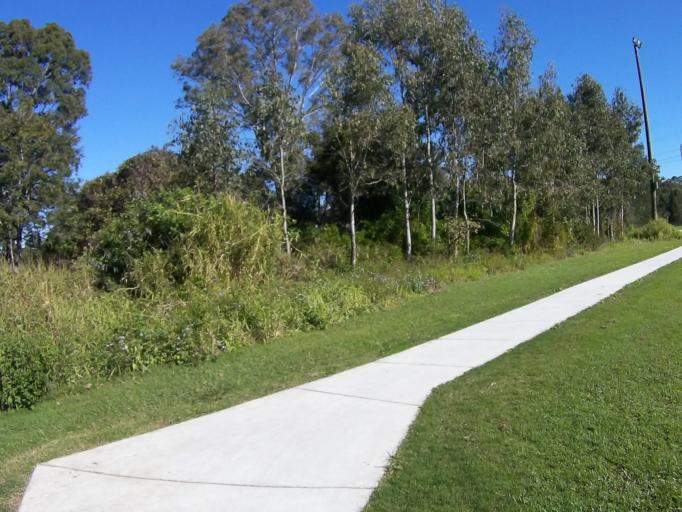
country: AU
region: Queensland
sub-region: Logan
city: Windaroo
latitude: -27.7374
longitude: 153.1960
